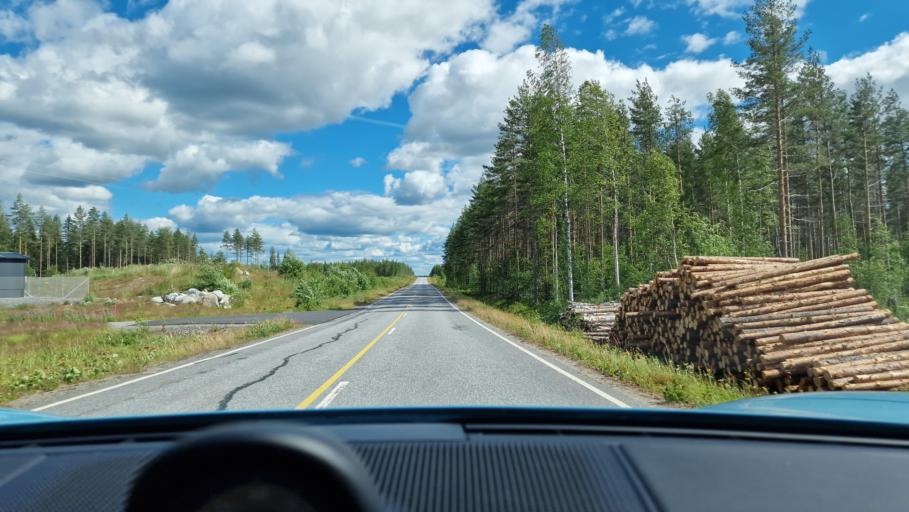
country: FI
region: Central Finland
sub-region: Saarijaervi-Viitasaari
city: Pylkoenmaeki
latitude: 62.6638
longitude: 24.5501
